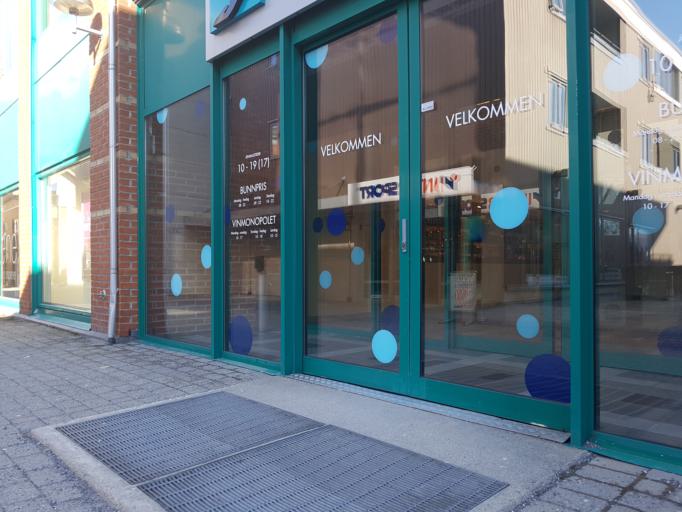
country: NO
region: Nordland
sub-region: Vefsn
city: Mosjoen
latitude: 65.8397
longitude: 13.1922
